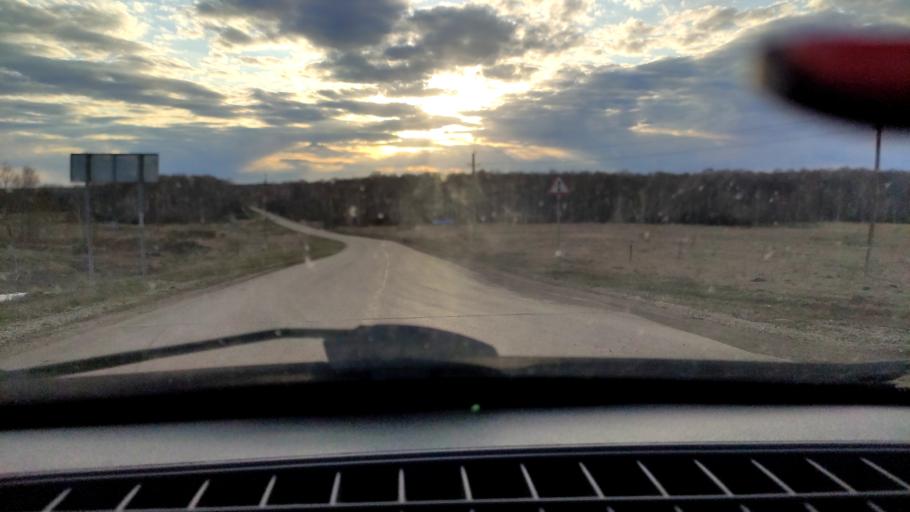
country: RU
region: Bashkortostan
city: Tolbazy
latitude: 54.0177
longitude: 55.7171
